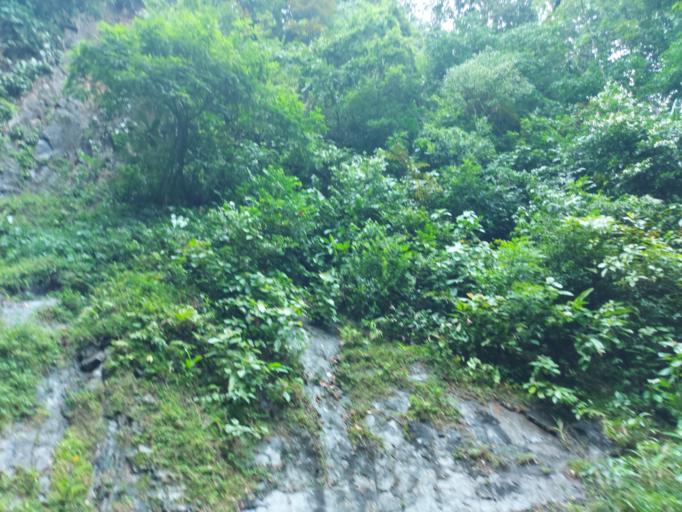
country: PA
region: Bocas del Toro
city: Barranco
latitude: 9.6287
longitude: -82.7737
